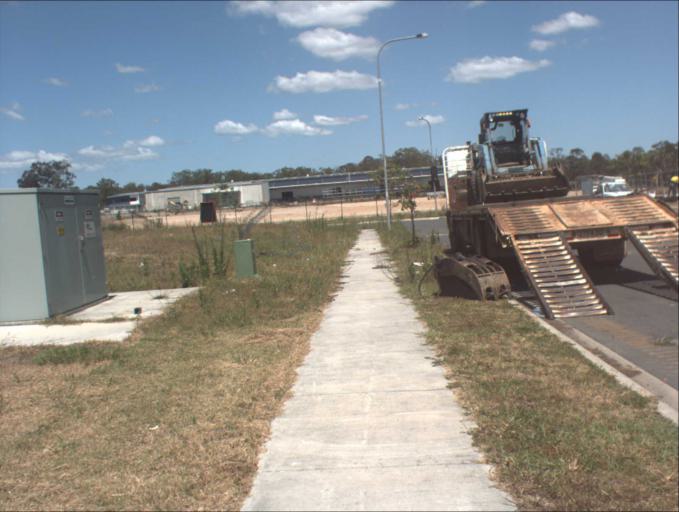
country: AU
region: Queensland
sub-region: Logan
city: Woodridge
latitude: -27.6473
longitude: 153.0931
